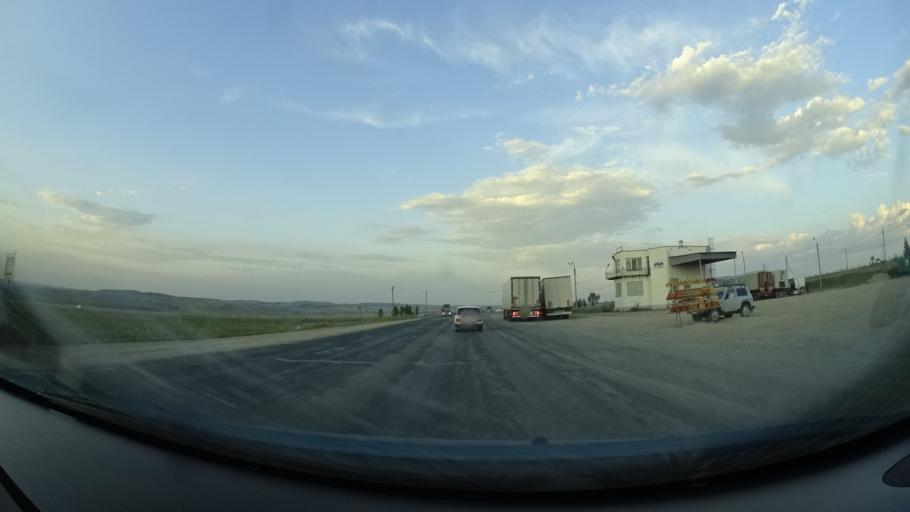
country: RU
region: Orenburg
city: Severnoye
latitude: 54.1153
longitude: 52.5231
